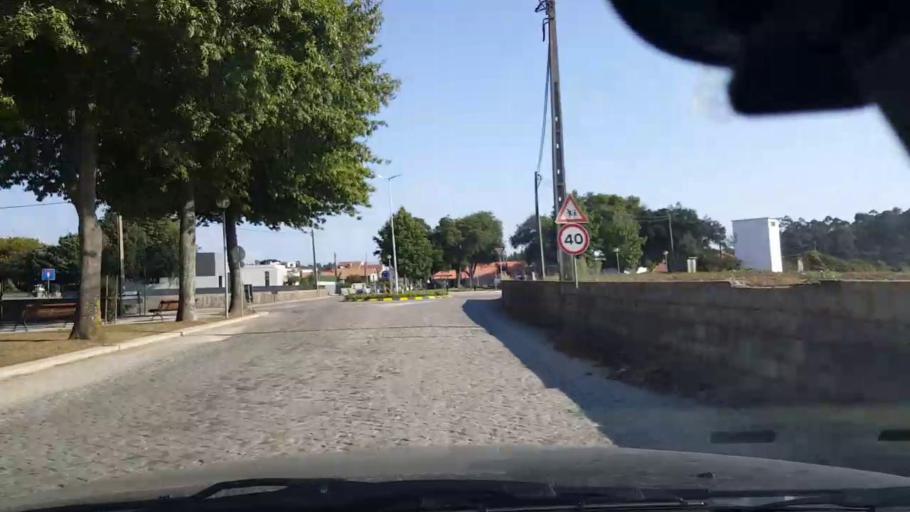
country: PT
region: Porto
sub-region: Vila do Conde
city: Arvore
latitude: 41.3510
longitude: -8.7187
